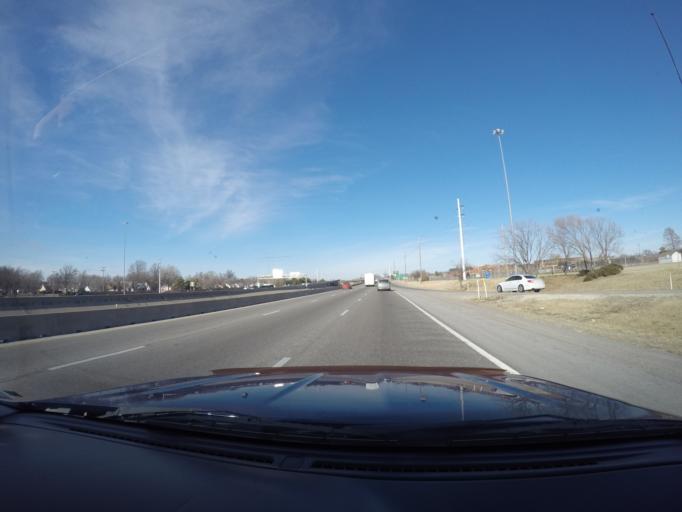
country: US
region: Kansas
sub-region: Sedgwick County
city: Wichita
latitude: 37.6814
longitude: -97.3123
